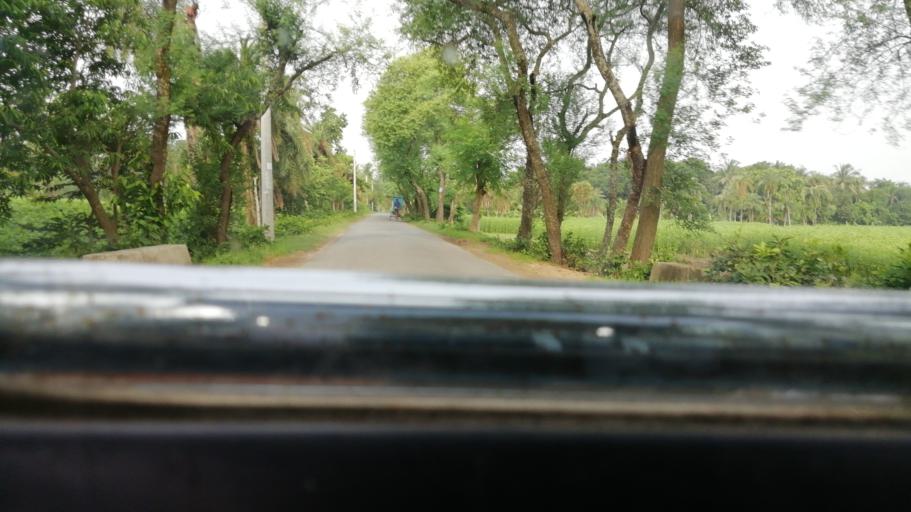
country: BD
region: Khulna
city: Kesabpur
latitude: 23.0270
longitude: 89.2640
